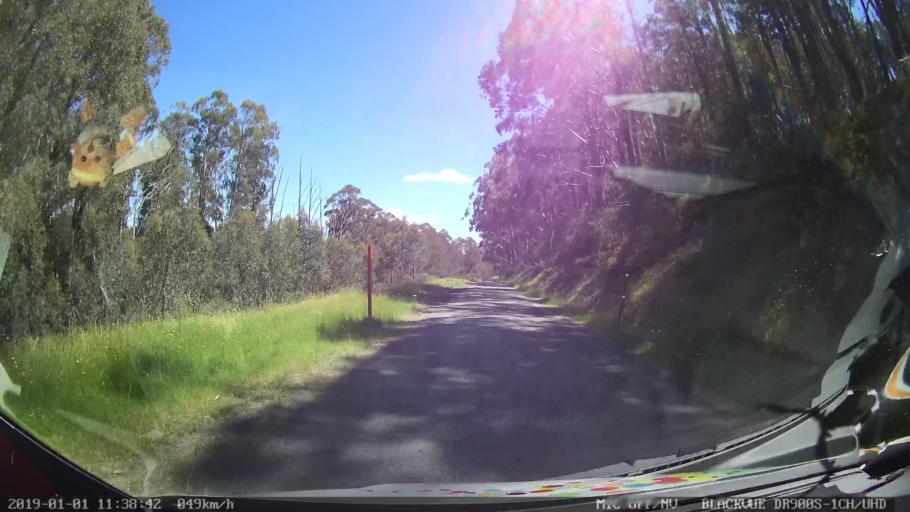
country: AU
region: New South Wales
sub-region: Snowy River
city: Jindabyne
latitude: -35.9325
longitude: 148.3867
